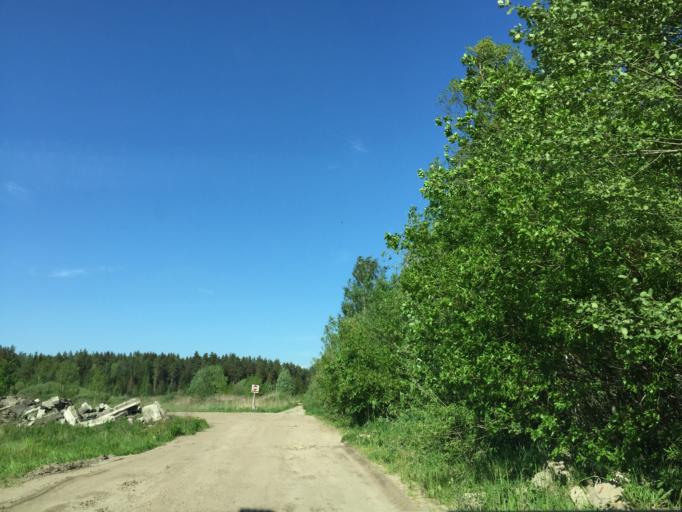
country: LV
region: Ozolnieku
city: Ozolnieki
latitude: 56.6679
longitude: 23.8076
